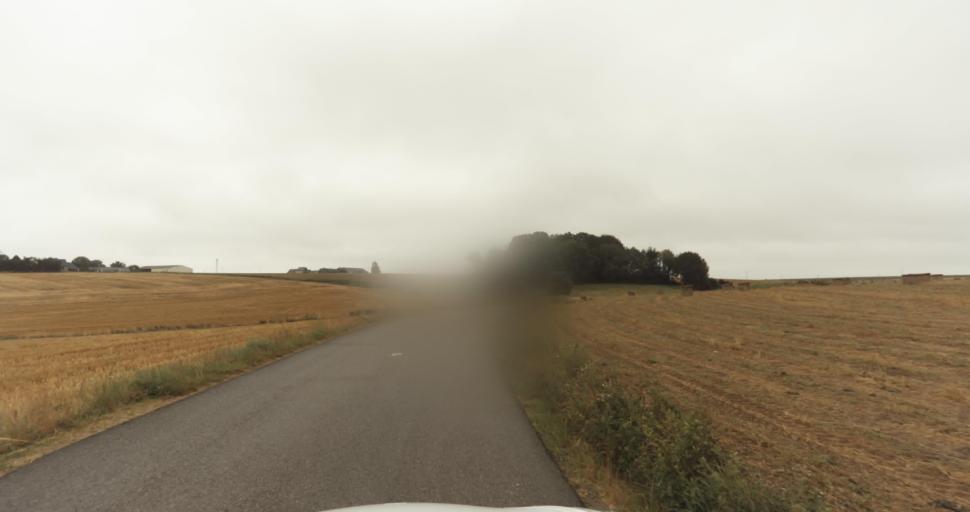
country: FR
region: Haute-Normandie
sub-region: Departement de l'Eure
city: Gravigny
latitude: 49.0767
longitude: 1.2186
